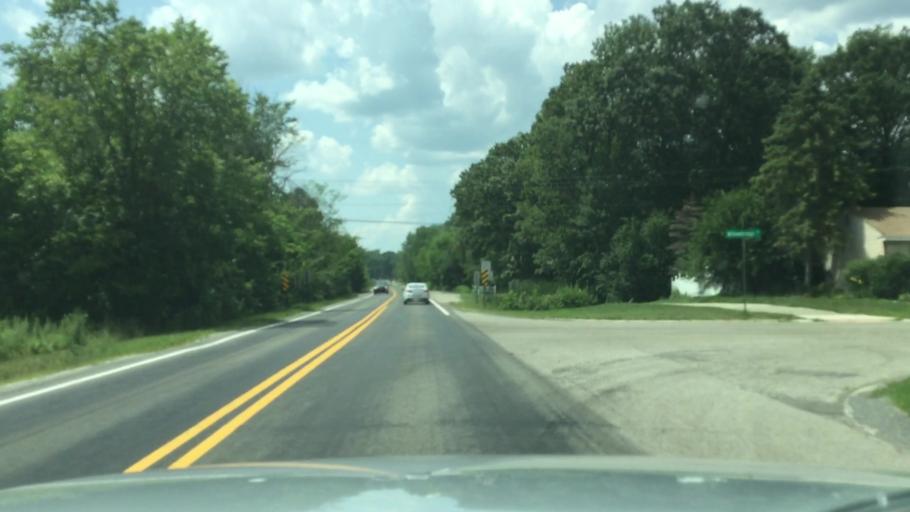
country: US
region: Michigan
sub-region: Washtenaw County
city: Ypsilanti
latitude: 42.2032
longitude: -83.5909
